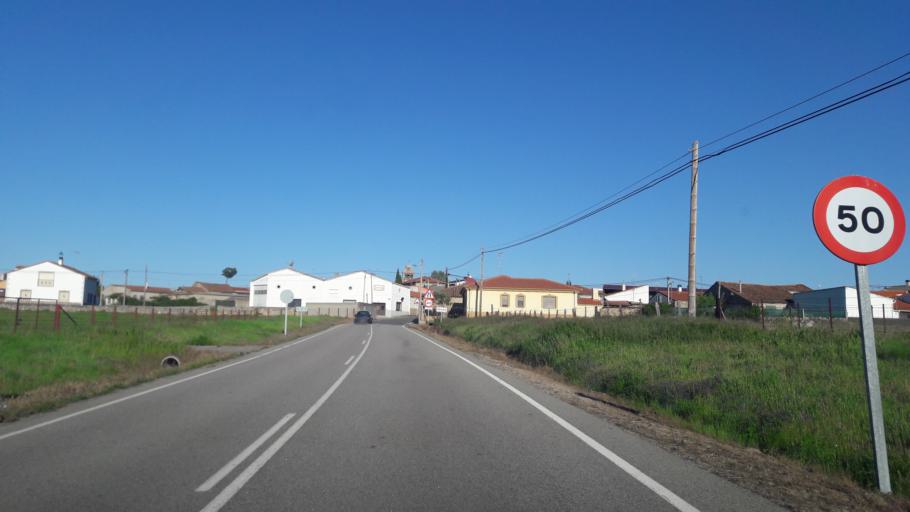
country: ES
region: Castille and Leon
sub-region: Provincia de Salamanca
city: Boada
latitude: 40.8155
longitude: -6.3024
